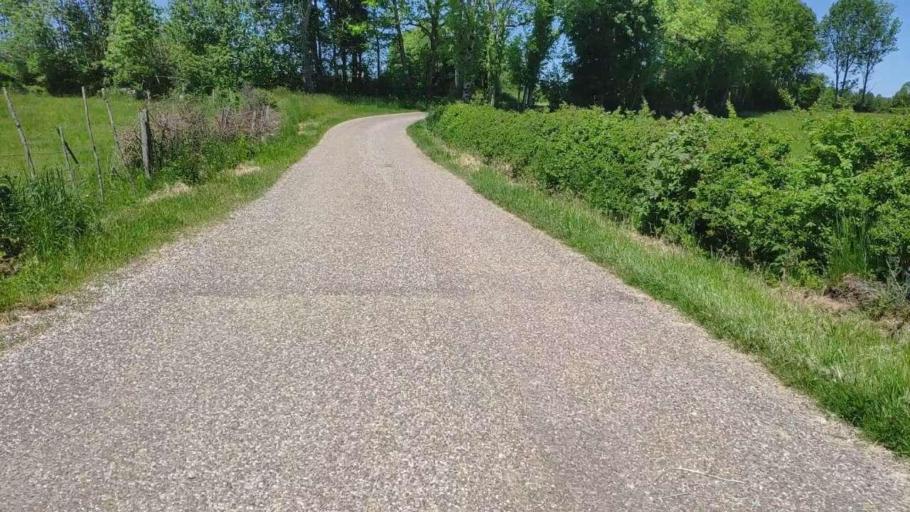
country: FR
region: Franche-Comte
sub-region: Departement du Jura
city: Perrigny
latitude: 46.7198
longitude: 5.6550
